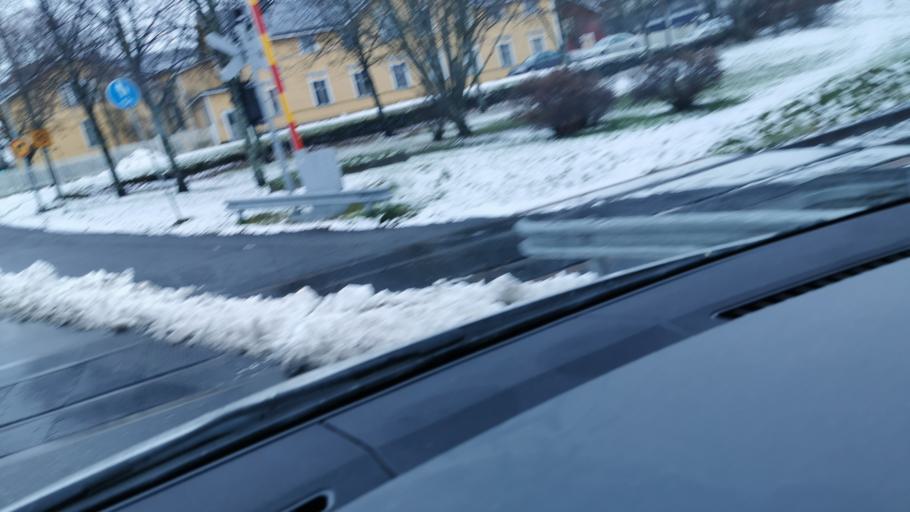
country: FI
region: Ostrobothnia
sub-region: Vaasa
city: Vaasa
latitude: 63.1011
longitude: 21.6040
